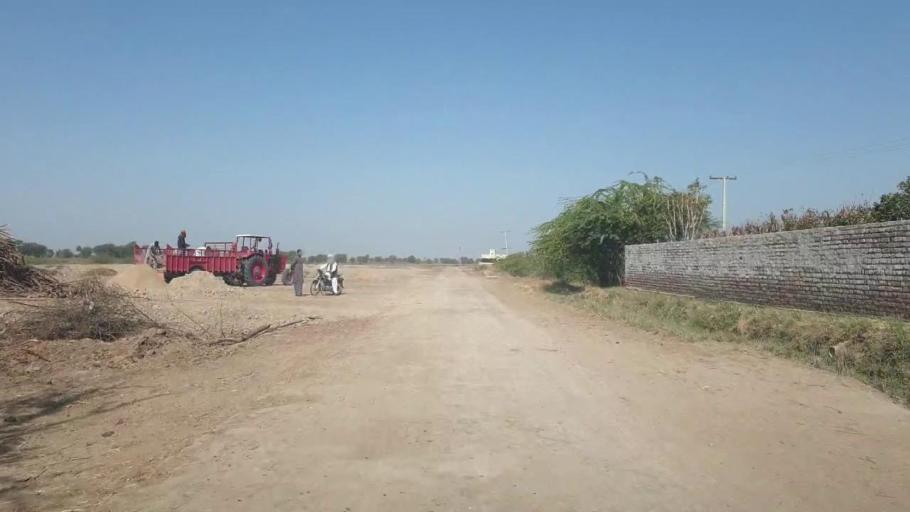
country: PK
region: Sindh
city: Umarkot
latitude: 25.3056
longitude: 69.6152
